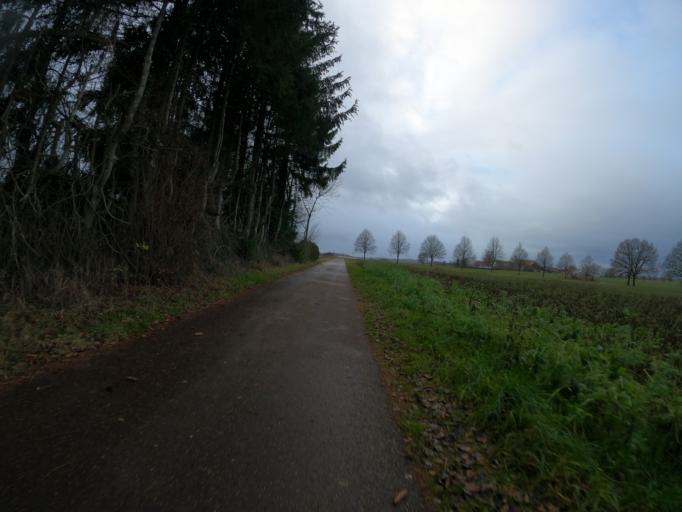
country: DE
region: Baden-Wuerttemberg
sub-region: Regierungsbezirk Stuttgart
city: Waschenbeuren
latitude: 48.7670
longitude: 9.6999
